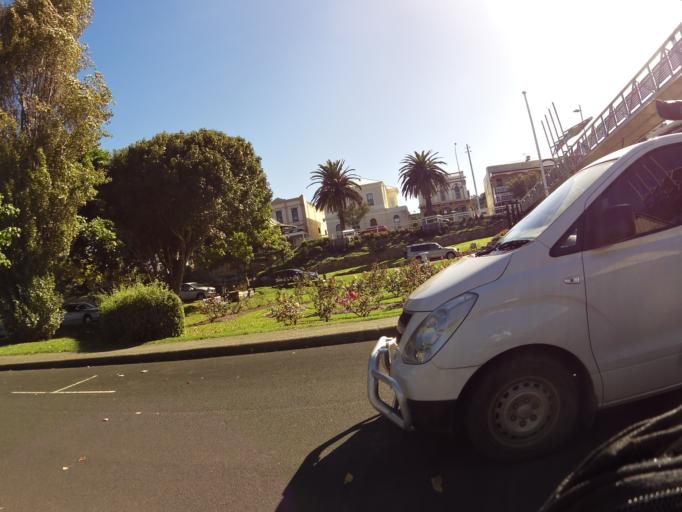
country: AU
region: Western Australia
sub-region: Albany
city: Albany
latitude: -35.0278
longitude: 117.8856
